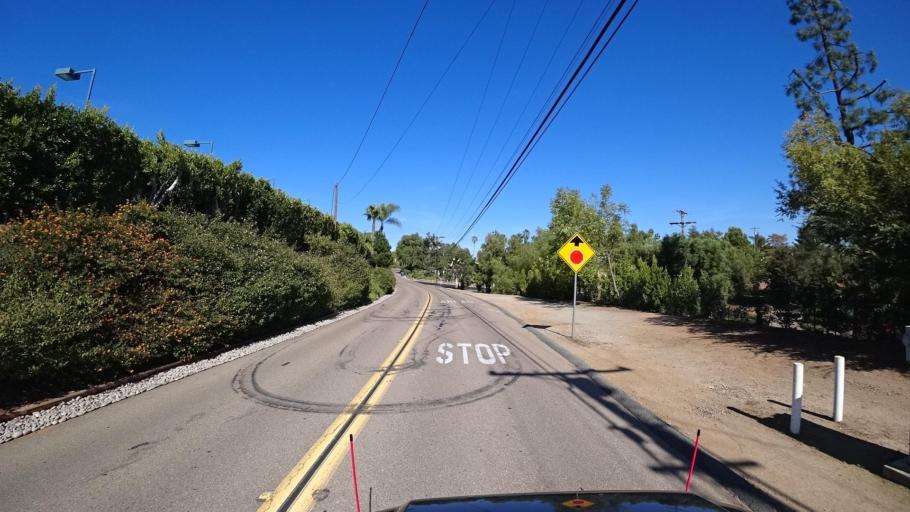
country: US
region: California
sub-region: San Diego County
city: Casa de Oro-Mount Helix
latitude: 32.7630
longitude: -116.9757
